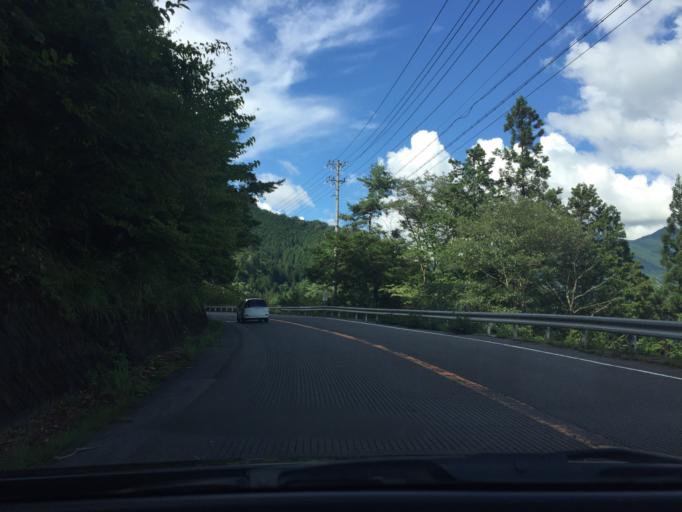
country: JP
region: Gifu
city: Nakatsugawa
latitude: 35.6804
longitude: 137.4116
